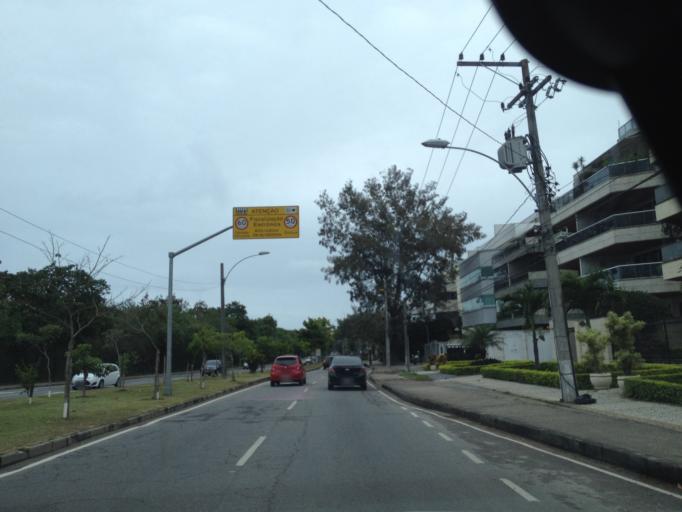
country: BR
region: Rio de Janeiro
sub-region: Nilopolis
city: Nilopolis
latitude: -23.0142
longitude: -43.4463
